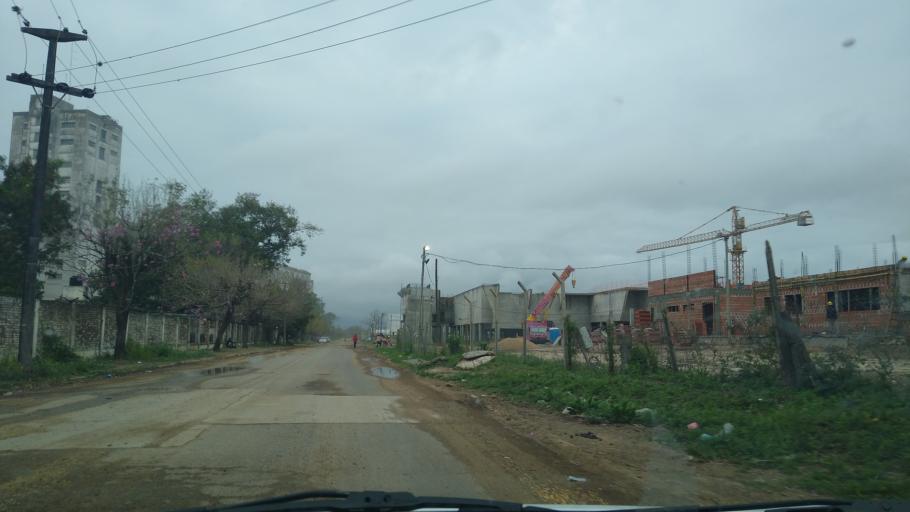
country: AR
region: Chaco
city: Barranqueras
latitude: -27.4713
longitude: -58.9091
